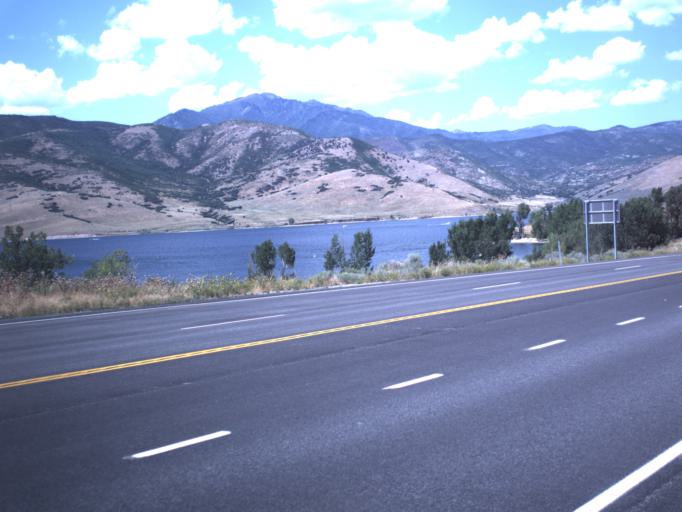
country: US
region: Utah
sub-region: Wasatch County
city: Midway
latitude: 40.4250
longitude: -111.4897
